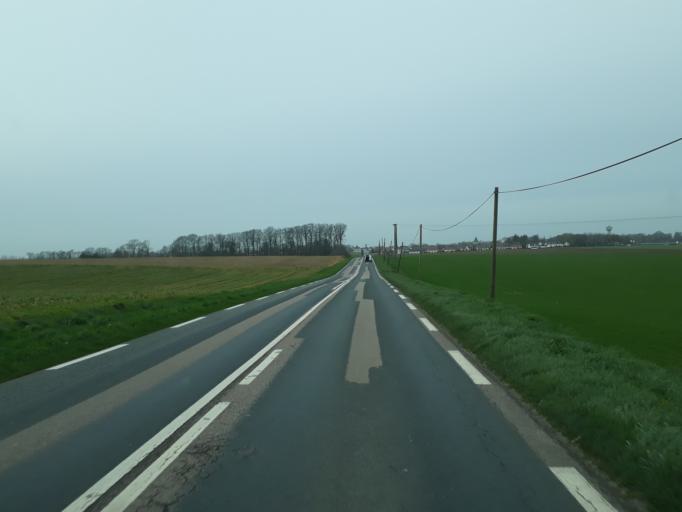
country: FR
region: Haute-Normandie
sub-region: Departement de la Seine-Maritime
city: Breaute
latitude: 49.6165
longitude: 0.4067
